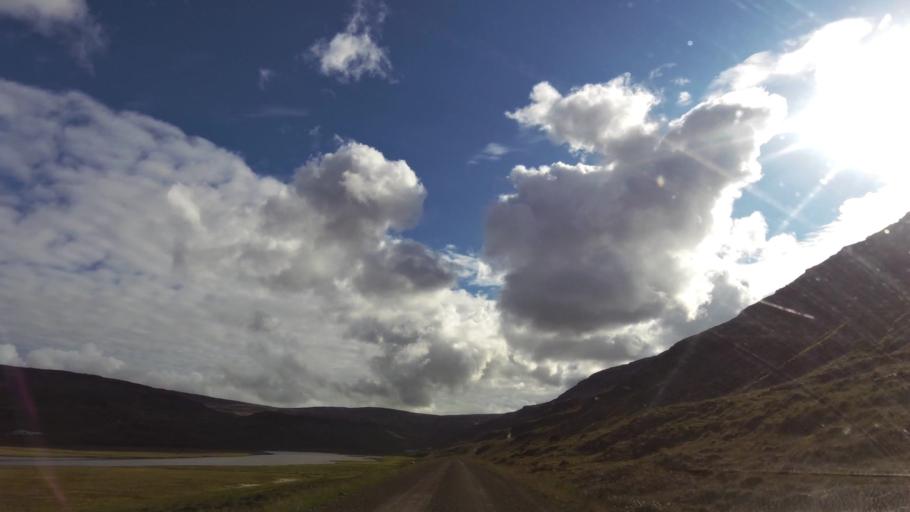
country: IS
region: West
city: Olafsvik
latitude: 65.5738
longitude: -24.1572
